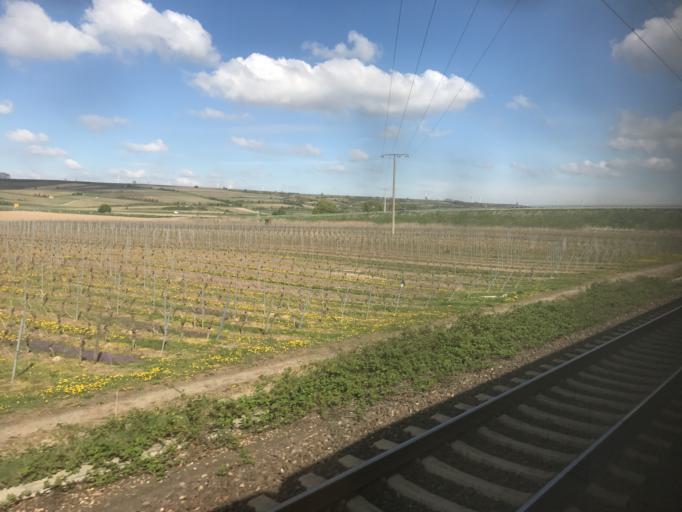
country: DE
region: Rheinland-Pfalz
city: Mettenheim
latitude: 49.7255
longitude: 8.3295
